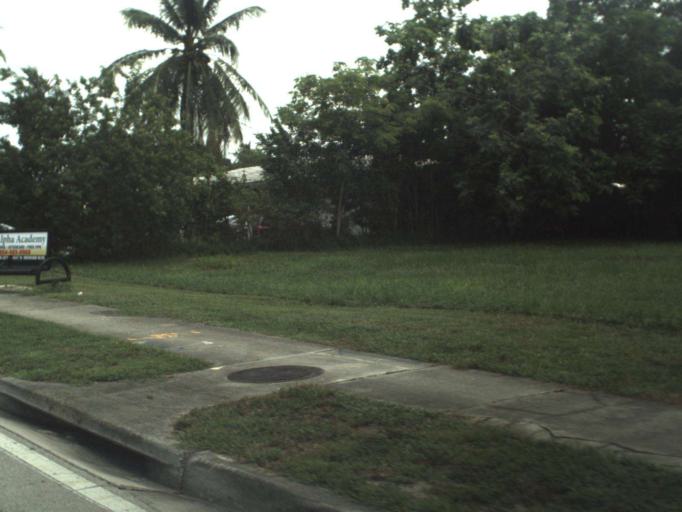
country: US
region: Florida
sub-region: Broward County
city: Lauderhill
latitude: 26.1208
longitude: -80.2143
